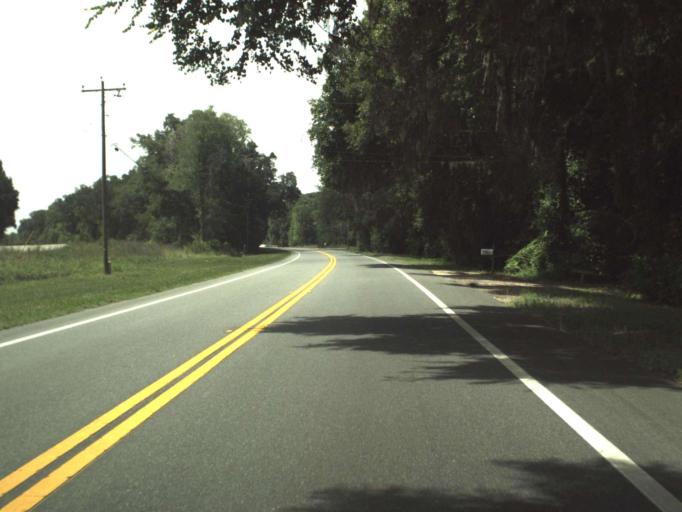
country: US
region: Florida
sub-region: Hernando County
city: Ridge Manor
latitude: 28.5777
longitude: -82.1542
